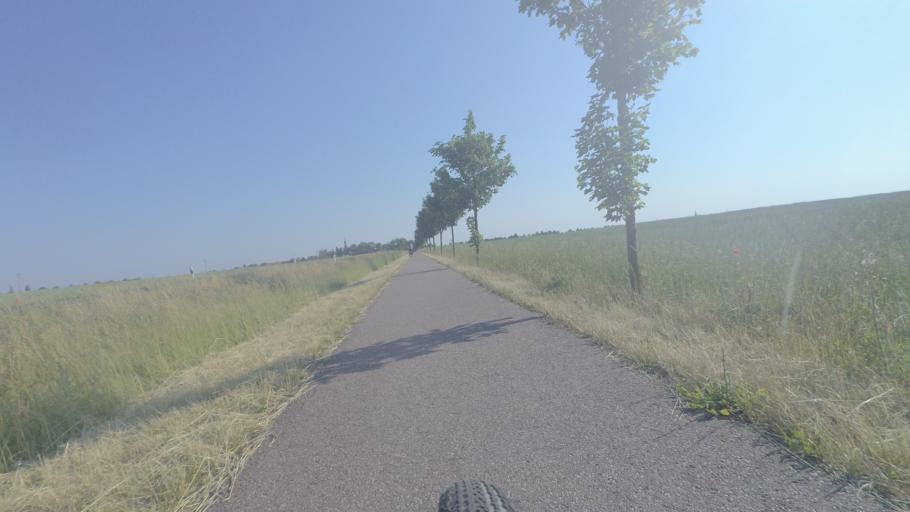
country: DE
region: Saxony-Anhalt
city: Osternienburger Land
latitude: 51.7861
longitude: 12.0081
